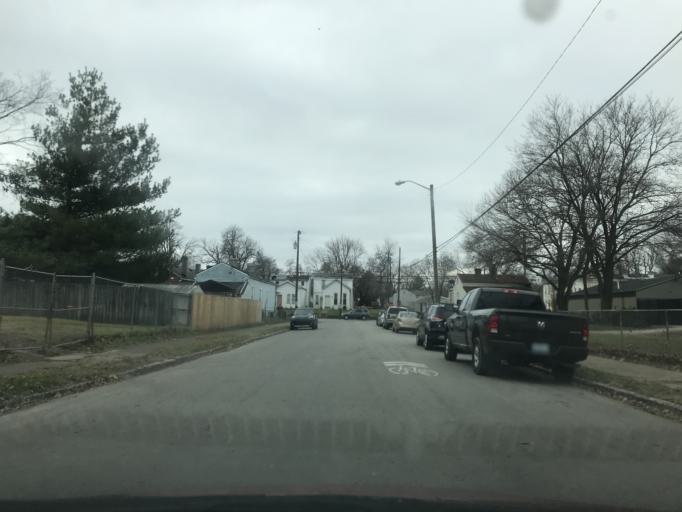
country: US
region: Kentucky
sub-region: Jefferson County
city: Louisville
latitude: 38.2690
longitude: -85.7877
